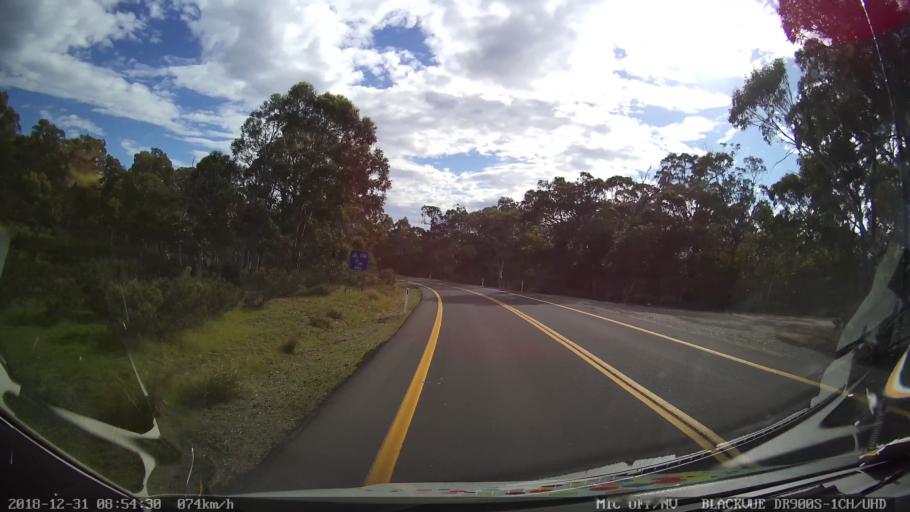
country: AU
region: New South Wales
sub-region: Snowy River
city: Jindabyne
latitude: -36.3536
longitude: 148.5620
